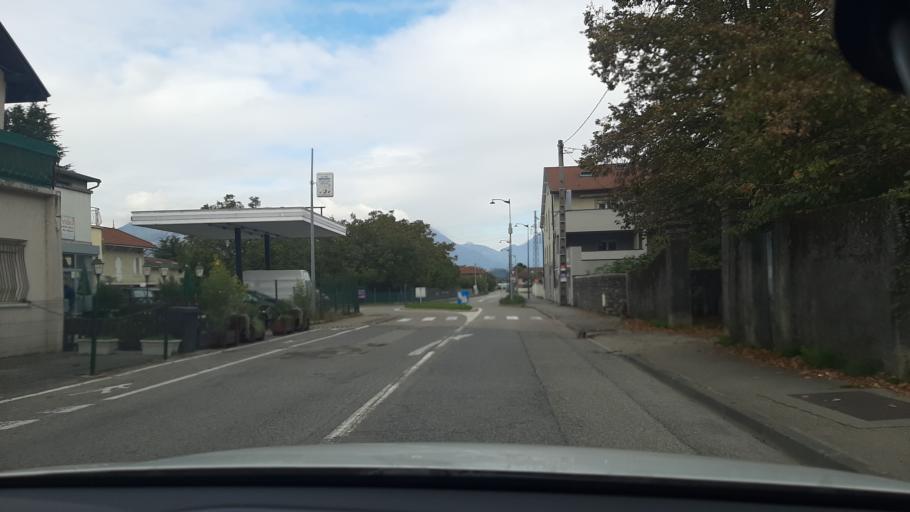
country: FR
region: Rhone-Alpes
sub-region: Departement de l'Isere
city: Pontcharra
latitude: 45.4361
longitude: 6.0266
